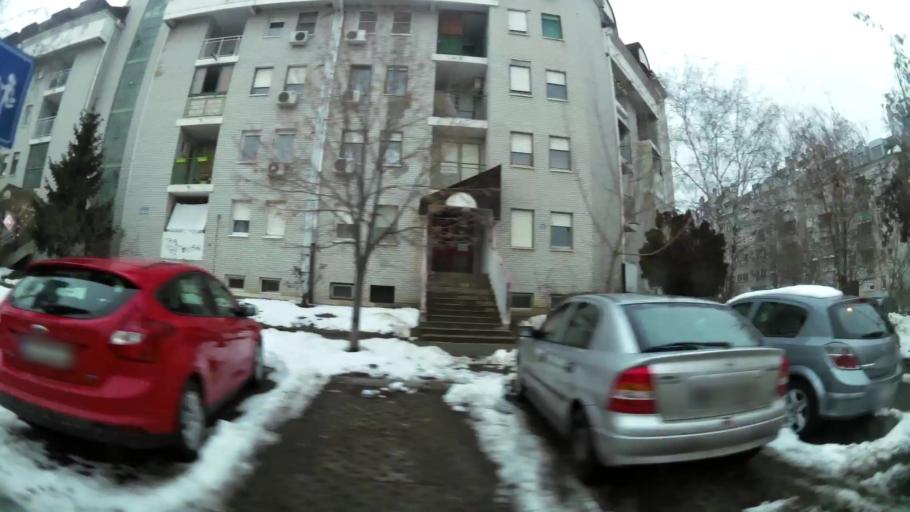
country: RS
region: Central Serbia
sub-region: Belgrade
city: Zemun
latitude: 44.8145
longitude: 20.3711
